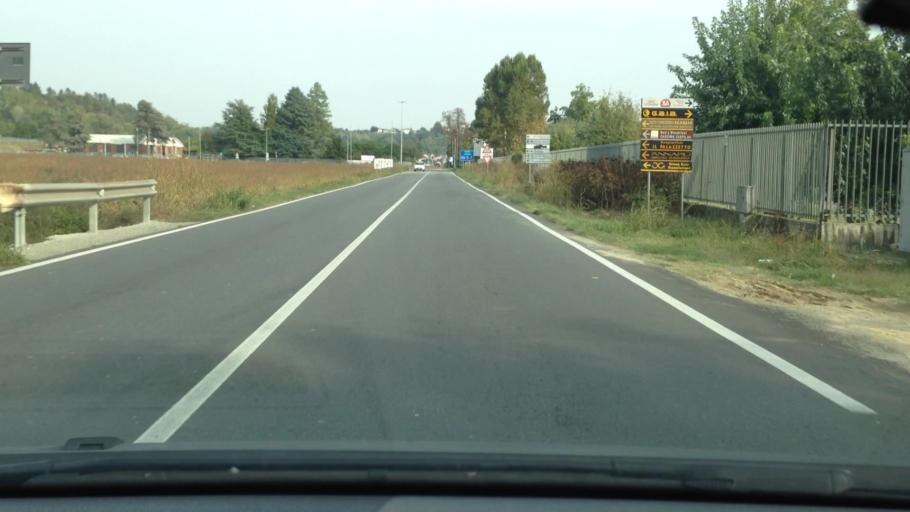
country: IT
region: Piedmont
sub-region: Provincia di Asti
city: Azzano d'Asti
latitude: 44.9069
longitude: 8.2696
